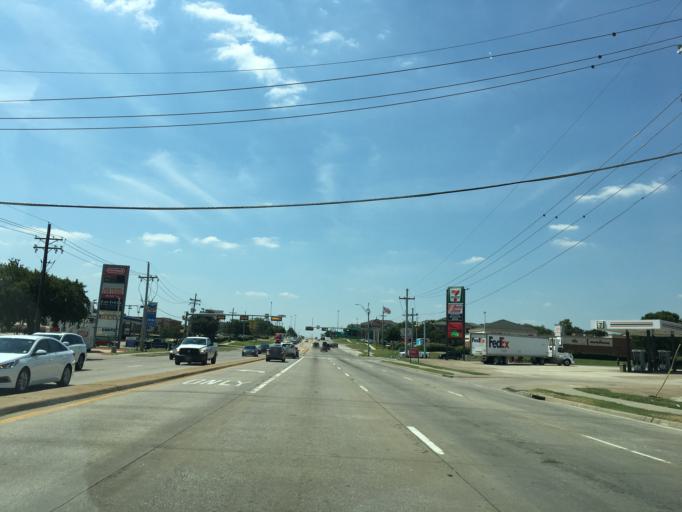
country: US
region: Texas
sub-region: Denton County
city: Lewisville
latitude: 33.0130
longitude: -96.9931
